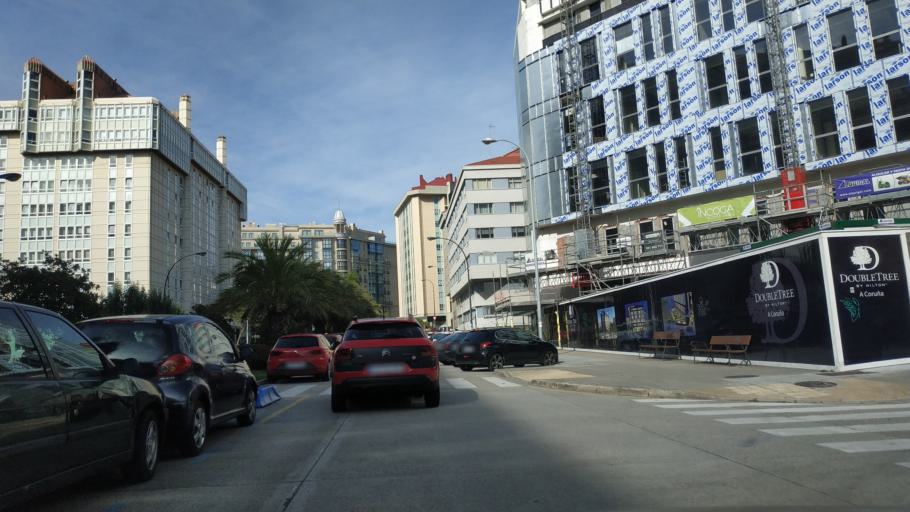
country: ES
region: Galicia
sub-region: Provincia da Coruna
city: A Coruna
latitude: 43.3737
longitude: -8.4005
